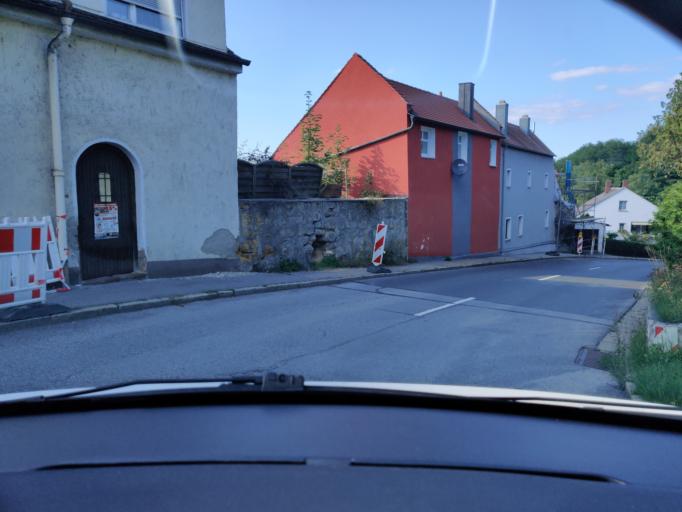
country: DE
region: Bavaria
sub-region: Upper Palatinate
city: Schwandorf in Bayern
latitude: 49.3305
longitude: 12.1095
